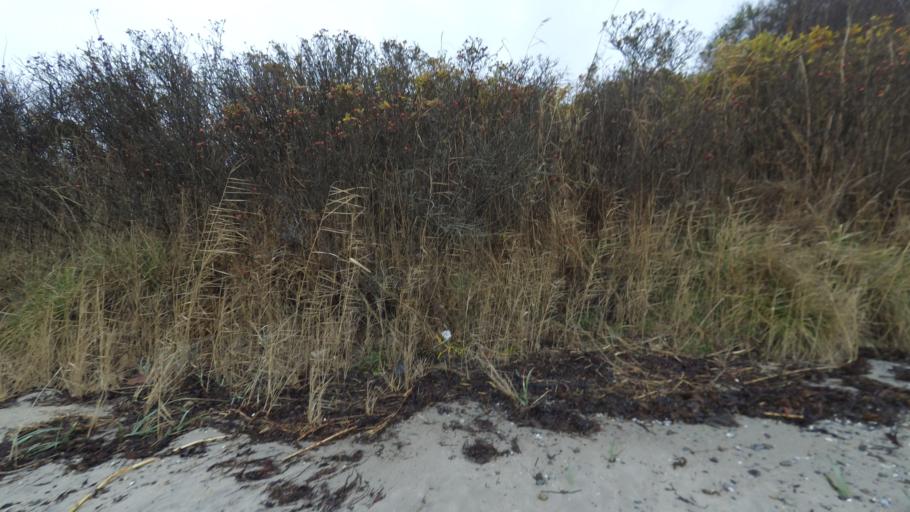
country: DK
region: Central Jutland
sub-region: Arhus Kommune
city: Malling
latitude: 55.9982
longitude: 10.2580
